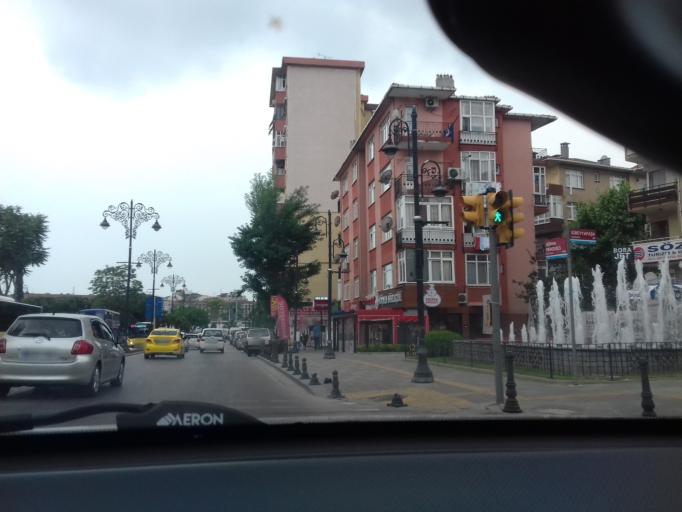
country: TR
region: Istanbul
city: Pendik
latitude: 40.8825
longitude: 29.2344
